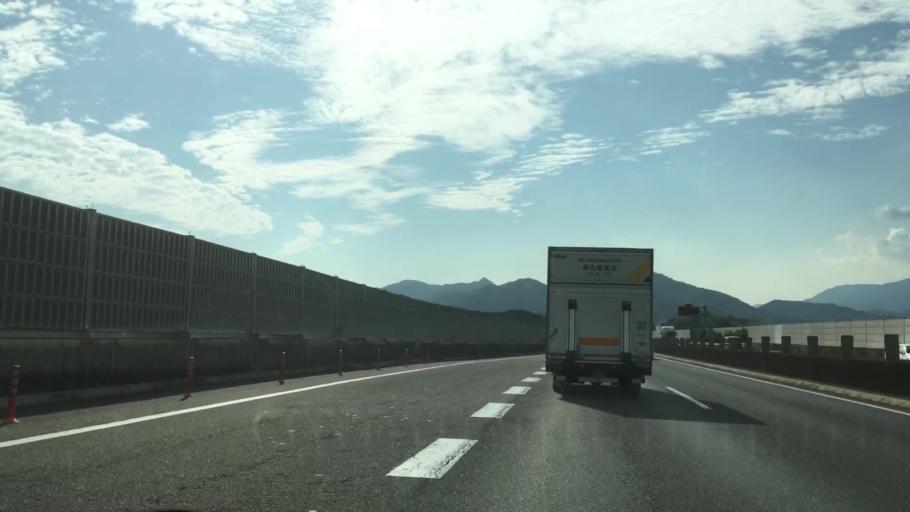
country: JP
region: Yamaguchi
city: Yanai
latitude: 34.0821
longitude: 132.0800
